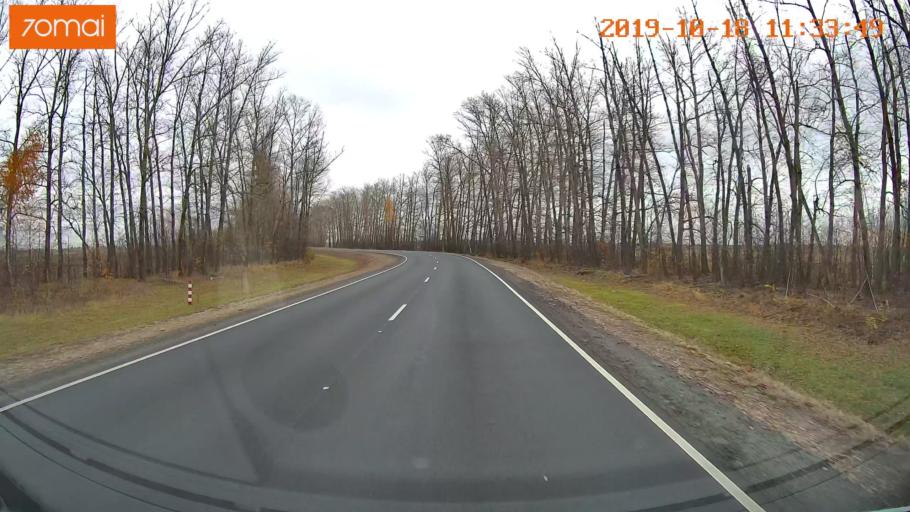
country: RU
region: Rjazan
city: Oktyabr'skiy
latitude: 54.1381
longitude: 38.7495
